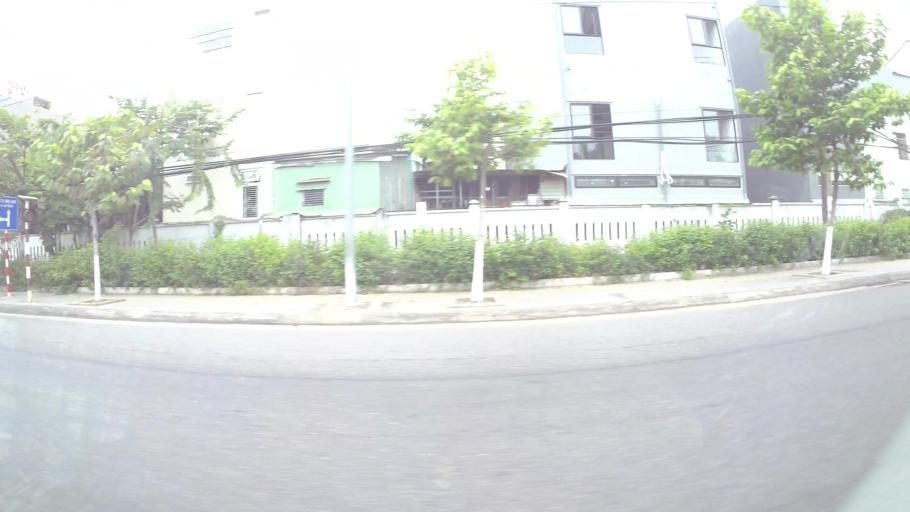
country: VN
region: Da Nang
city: Thanh Khe
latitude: 16.0538
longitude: 108.2043
